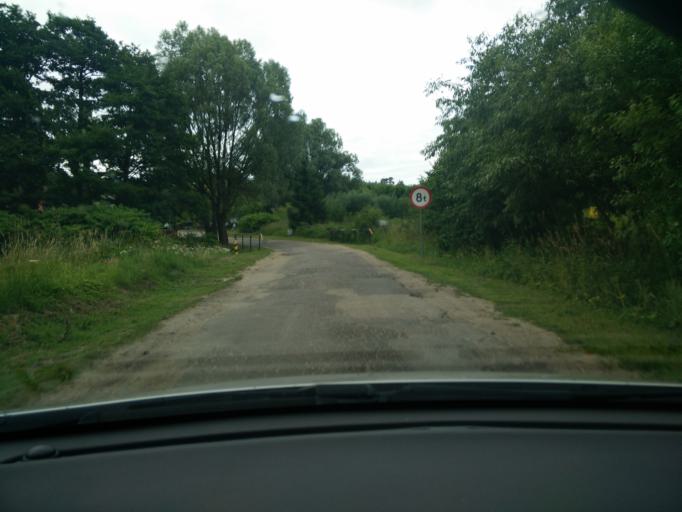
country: PL
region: Pomeranian Voivodeship
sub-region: Powiat pucki
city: Mrzezino
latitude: 54.6638
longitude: 18.4563
